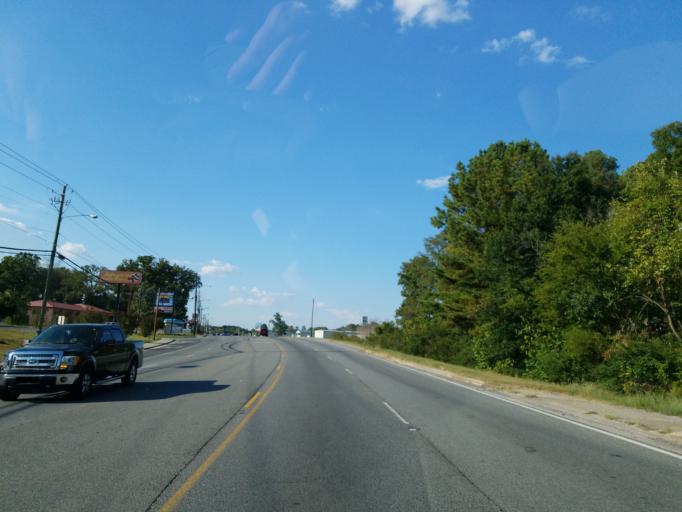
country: US
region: Georgia
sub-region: Murray County
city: Chatsworth
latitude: 34.7816
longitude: -84.7697
